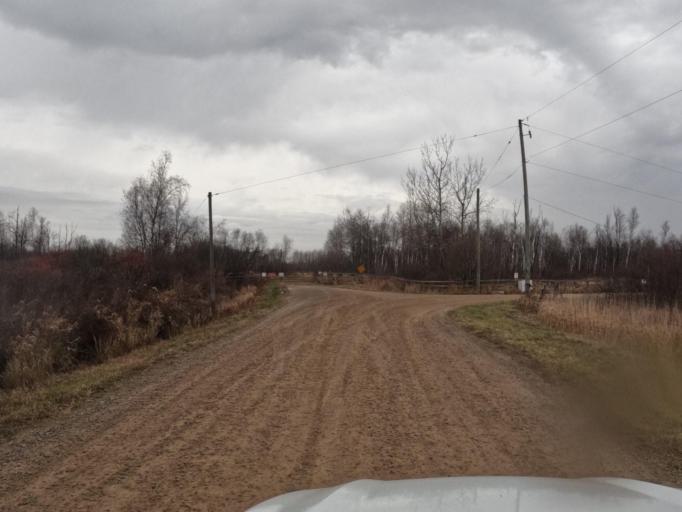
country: CA
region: Ontario
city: Shelburne
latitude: 43.8973
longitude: -80.3847
